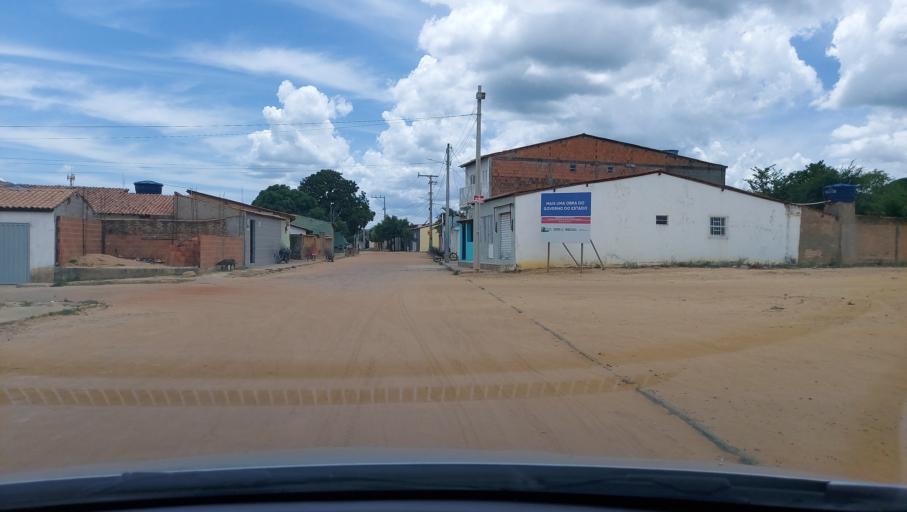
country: BR
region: Bahia
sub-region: Oliveira Dos Brejinhos
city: Beira Rio
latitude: -12.0014
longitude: -42.6294
